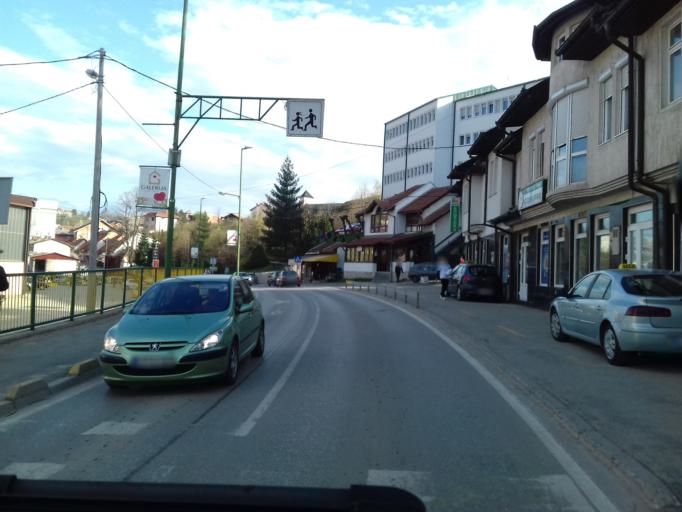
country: BA
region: Federation of Bosnia and Herzegovina
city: Tesanj
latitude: 44.6090
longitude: 17.9886
